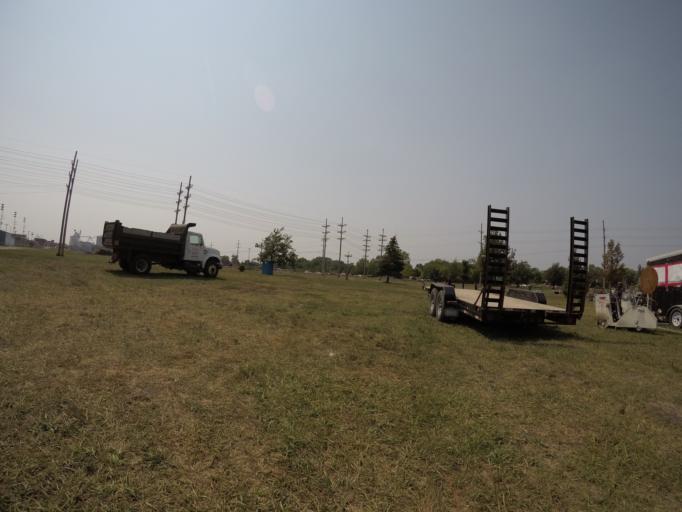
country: US
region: Nebraska
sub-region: Gage County
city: Beatrice
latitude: 40.2704
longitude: -96.7514
